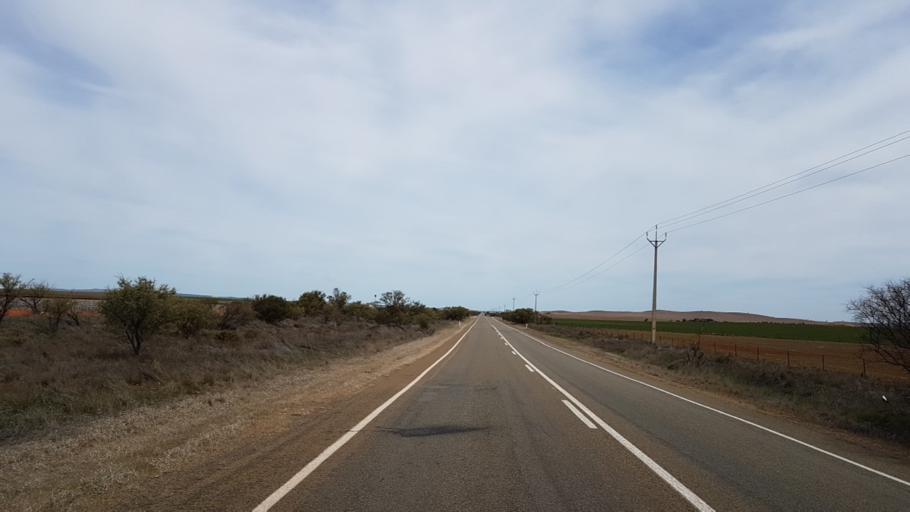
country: AU
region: South Australia
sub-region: Peterborough
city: Peterborough
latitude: -33.0019
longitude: 138.7761
